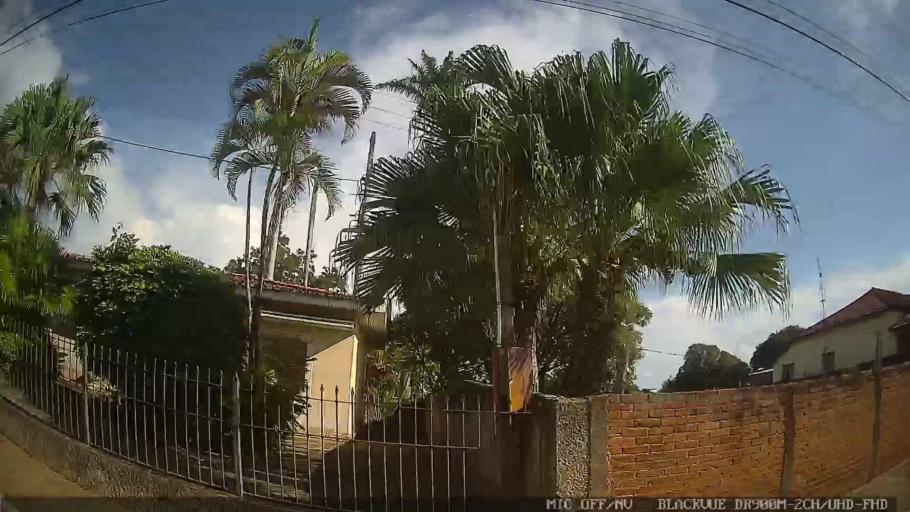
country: BR
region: Sao Paulo
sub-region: Laranjal Paulista
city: Laranjal Paulista
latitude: -23.0850
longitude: -47.7910
